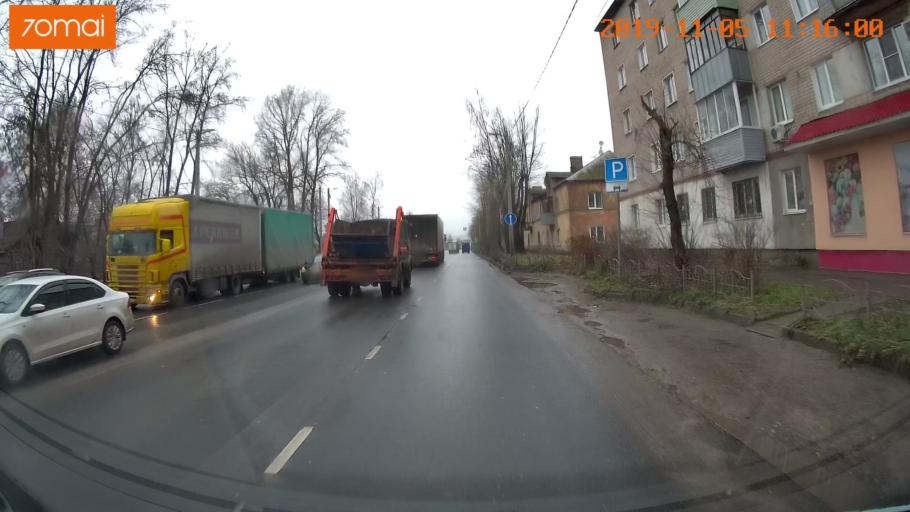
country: RU
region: Ivanovo
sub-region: Gorod Ivanovo
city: Ivanovo
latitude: 56.9811
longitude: 40.9537
